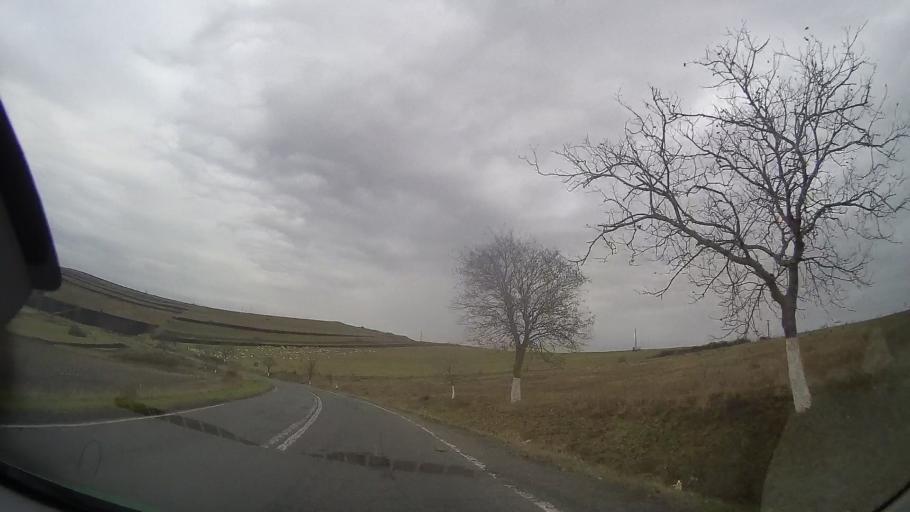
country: RO
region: Mures
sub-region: Comuna Faragau
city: Faragau
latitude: 46.7575
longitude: 24.5349
